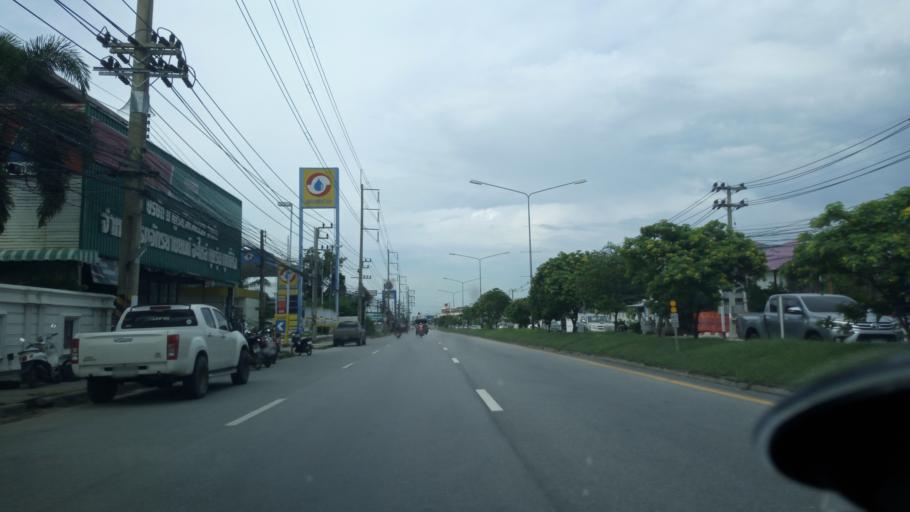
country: TH
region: Chon Buri
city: Chon Buri
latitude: 13.3904
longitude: 101.0195
